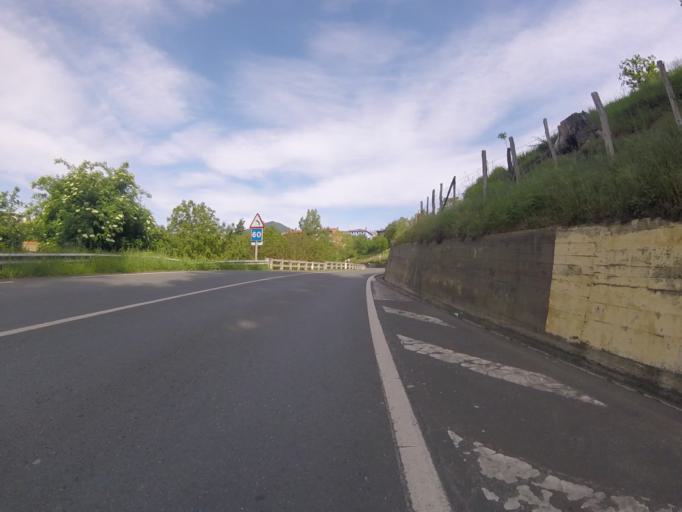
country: ES
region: Basque Country
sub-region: Provincia de Guipuzcoa
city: Zumarraga
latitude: 43.0856
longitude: -2.3068
